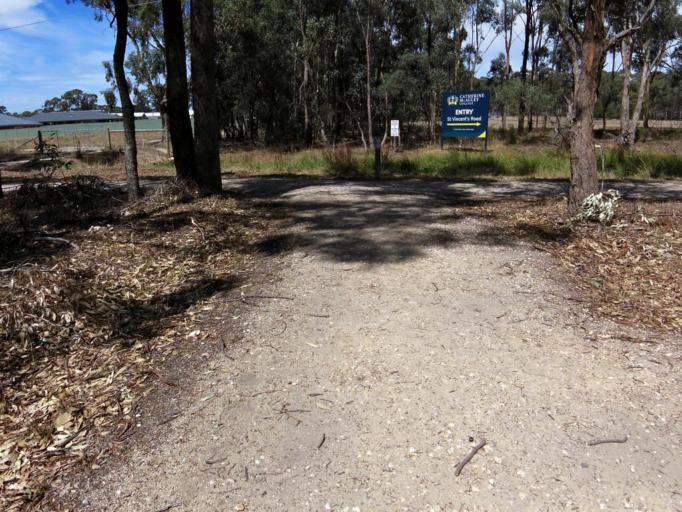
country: AU
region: Victoria
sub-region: Greater Bendigo
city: Kennington
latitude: -36.7704
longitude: 144.3453
